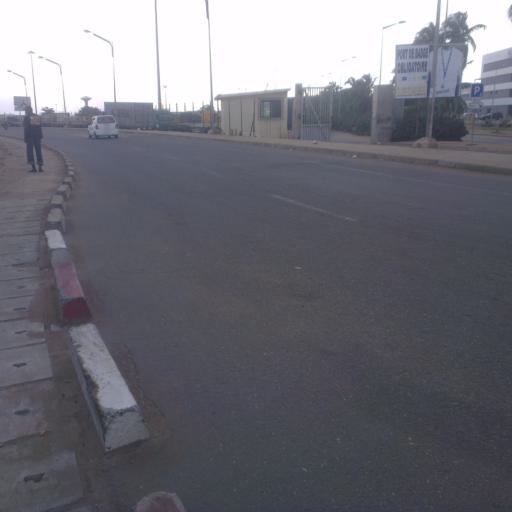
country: TG
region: Maritime
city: Lome
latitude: 6.1401
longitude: 1.2733
